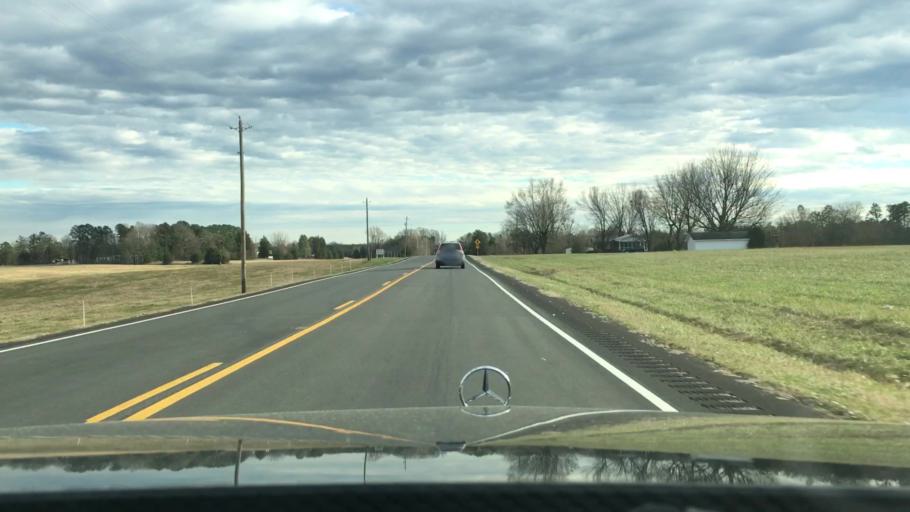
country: US
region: North Carolina
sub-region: Caswell County
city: Yanceyville
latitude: 36.3708
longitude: -79.2576
